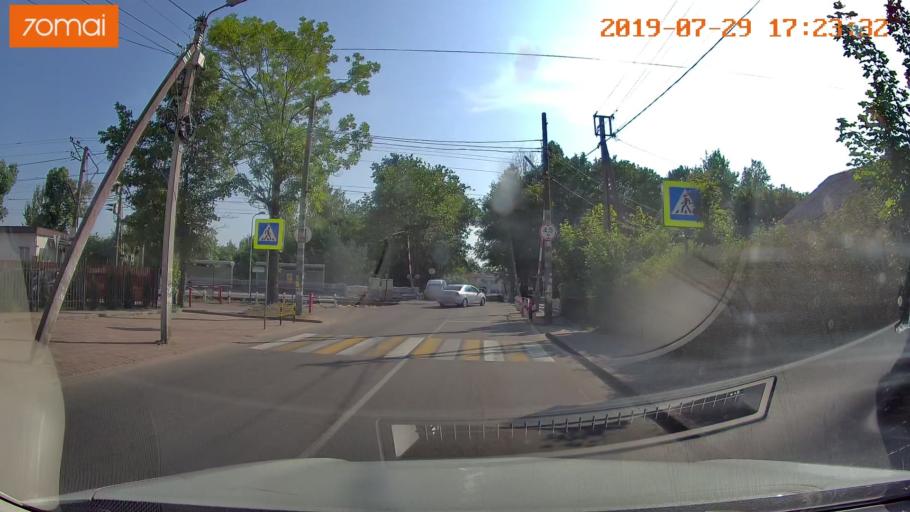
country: RU
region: Kaliningrad
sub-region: Gorod Kaliningrad
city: Kaliningrad
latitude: 54.7652
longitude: 20.4446
